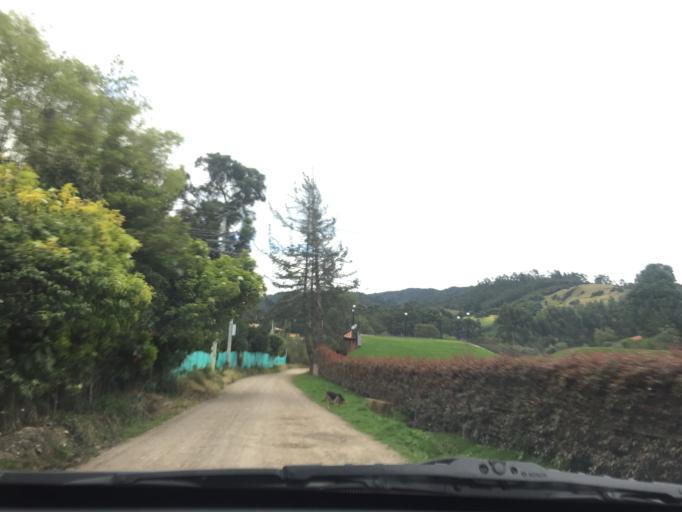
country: CO
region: Cundinamarca
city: Tabio
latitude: 4.9330
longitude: -74.1311
